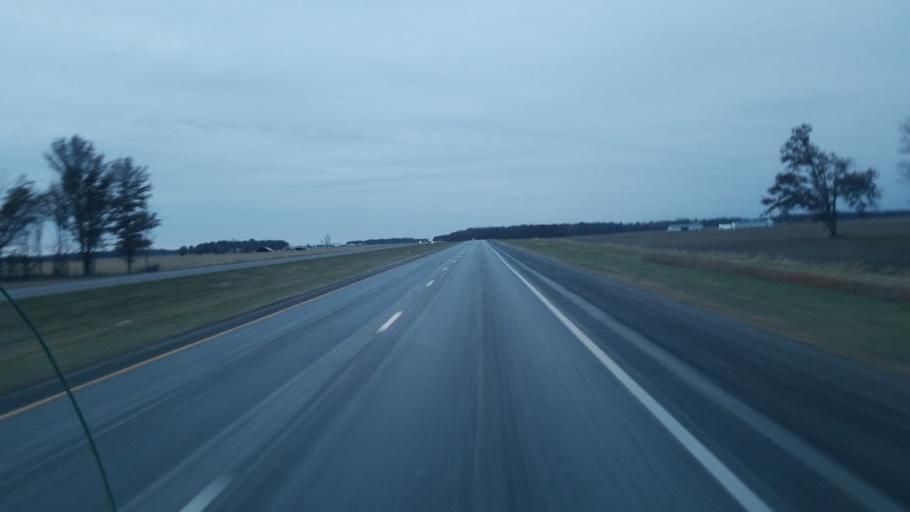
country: US
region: Ohio
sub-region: Hardin County
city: Ada
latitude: 40.8259
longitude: -83.7551
